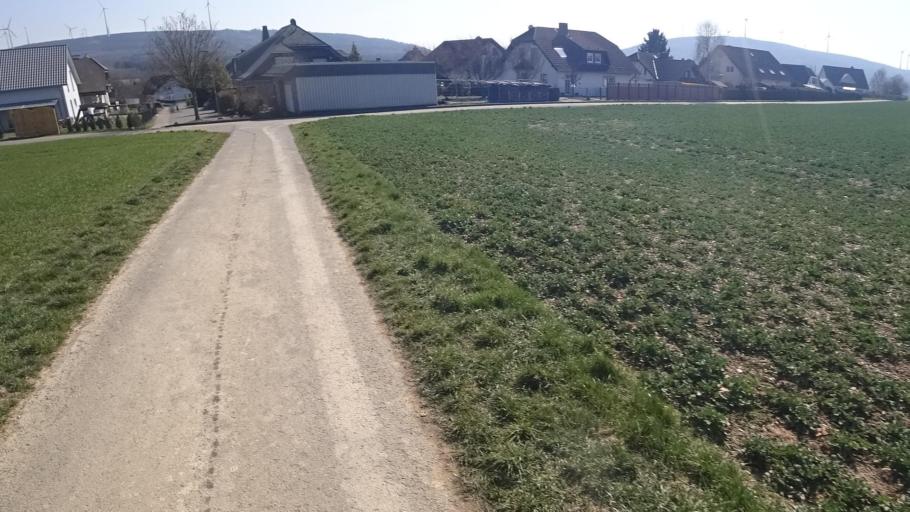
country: DE
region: Rheinland-Pfalz
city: Dichtelbach
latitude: 50.0098
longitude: 7.6887
